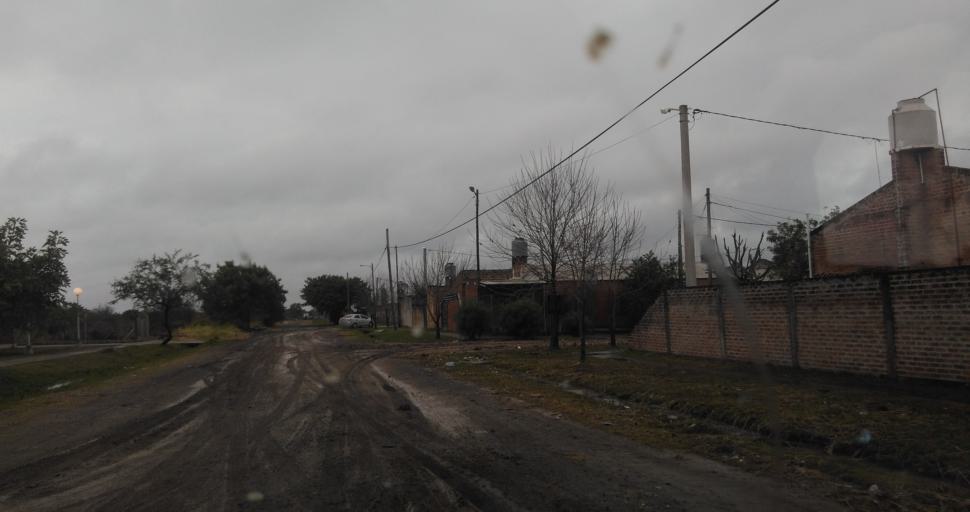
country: AR
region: Chaco
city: Fontana
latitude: -27.4558
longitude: -59.0448
